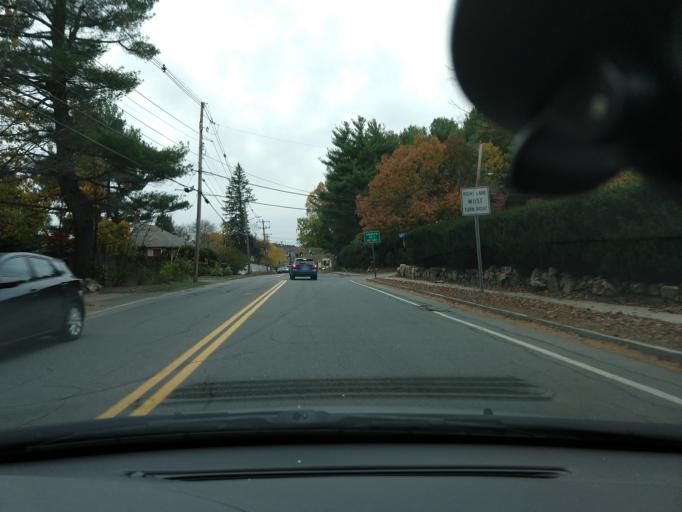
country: US
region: Massachusetts
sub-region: Middlesex County
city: Bedford
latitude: 42.4828
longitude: -71.2585
